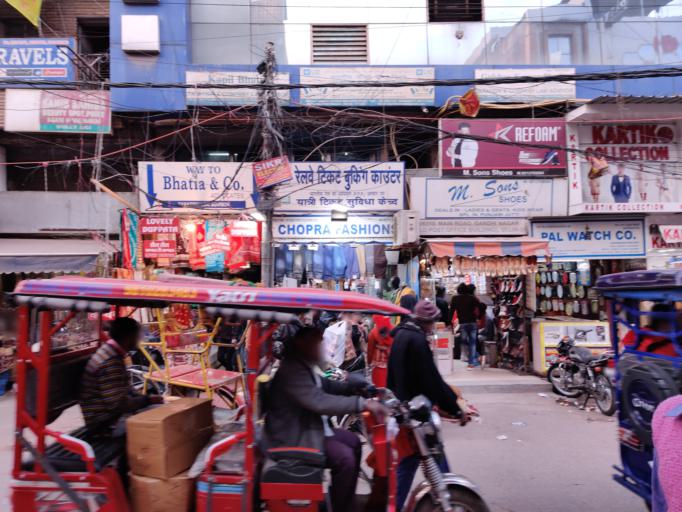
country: IN
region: NCT
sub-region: North Delhi
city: Delhi
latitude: 28.6605
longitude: 77.2653
